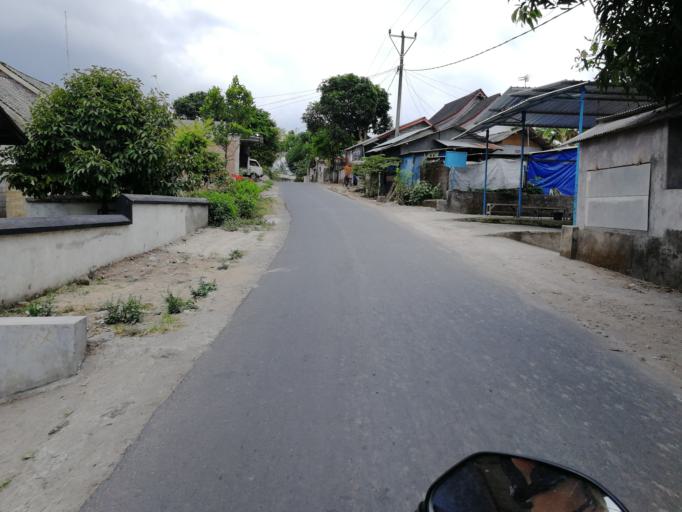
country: ID
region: West Nusa Tenggara
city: Pediti
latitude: -8.5694
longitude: 116.3298
